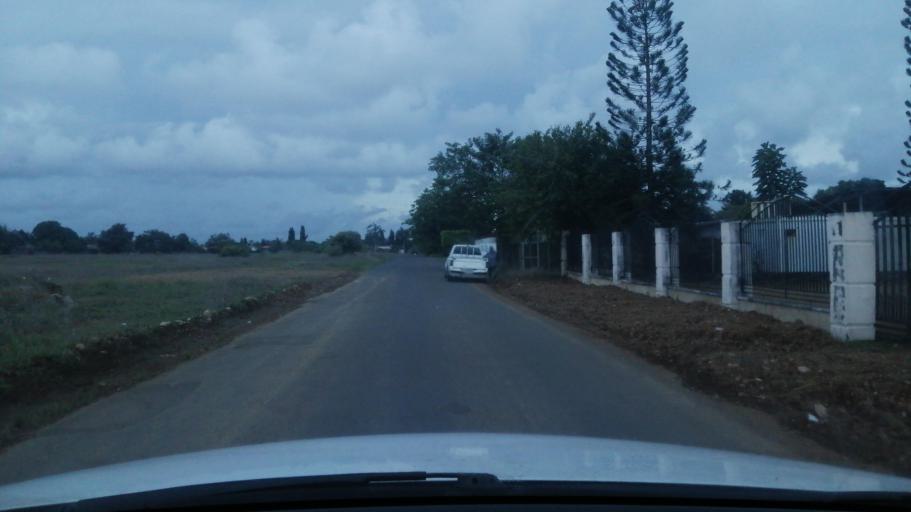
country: PA
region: Chiriqui
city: David
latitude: 8.4062
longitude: -82.4542
